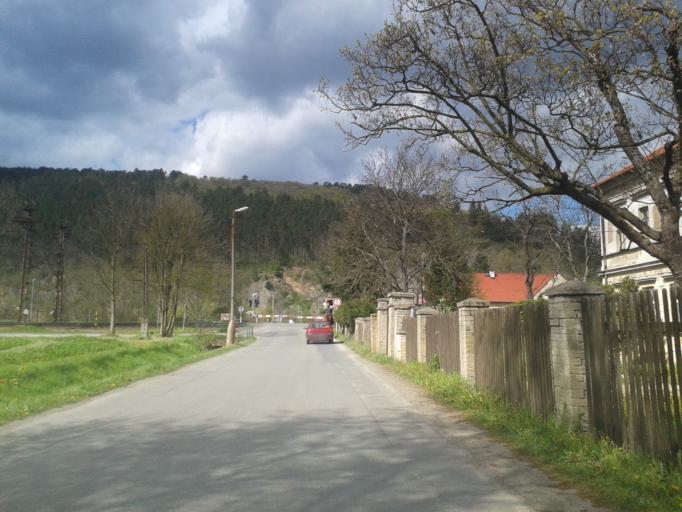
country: CZ
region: Central Bohemia
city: Revnice
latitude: 49.9316
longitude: 14.1797
